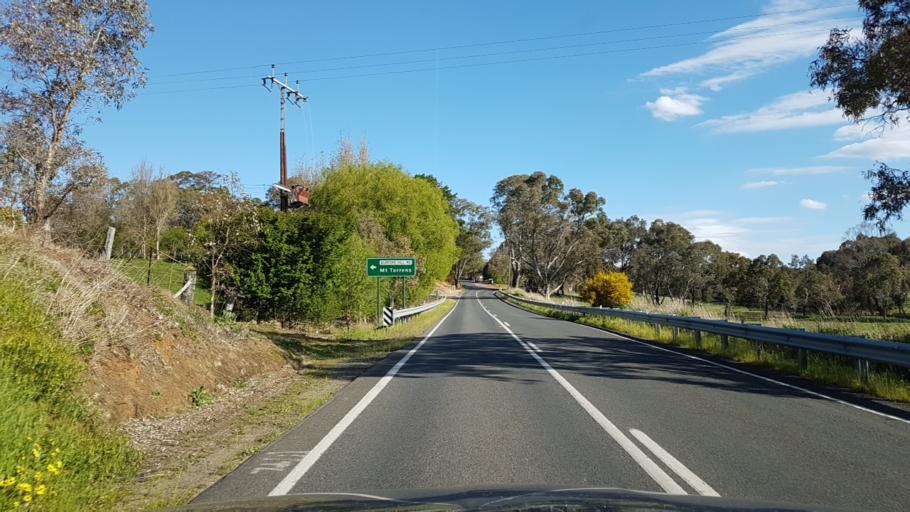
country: AU
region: South Australia
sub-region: Adelaide Hills
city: Gumeracha
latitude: -34.8529
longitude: 138.8938
